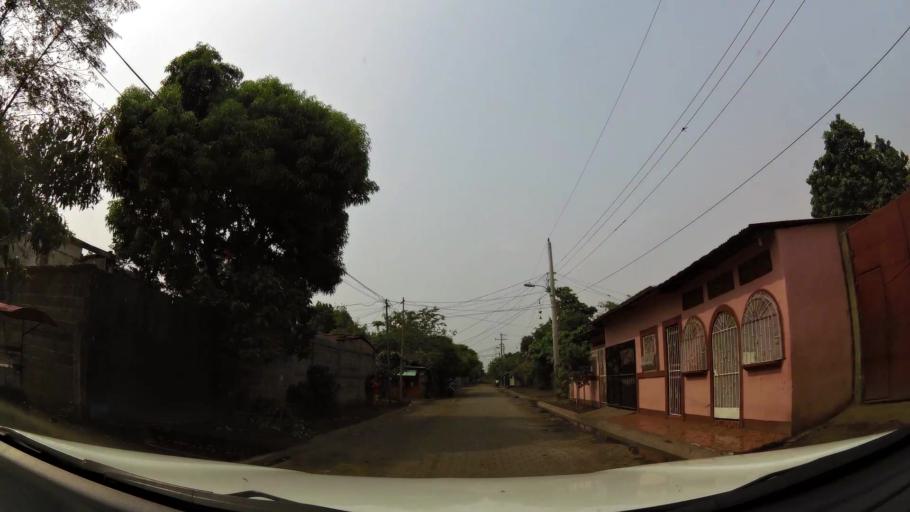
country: NI
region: Chinandega
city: Chinandega
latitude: 12.6294
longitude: -87.1453
